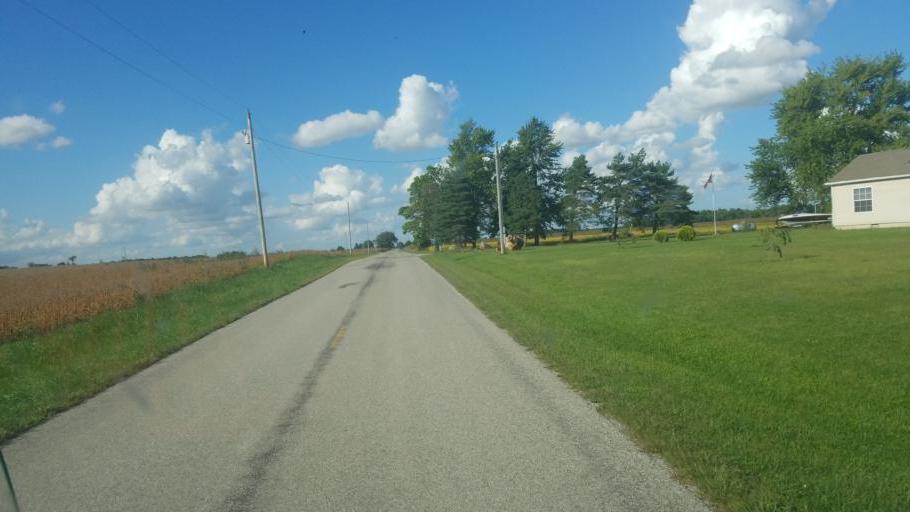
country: US
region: Ohio
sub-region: Hardin County
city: Kenton
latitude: 40.7153
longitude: -83.6917
